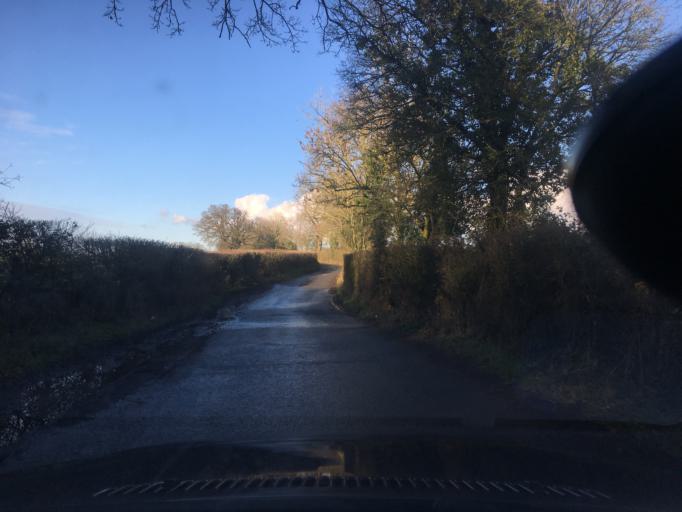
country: GB
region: England
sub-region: West Berkshire
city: Stratfield Mortimer
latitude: 51.3894
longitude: -1.0206
